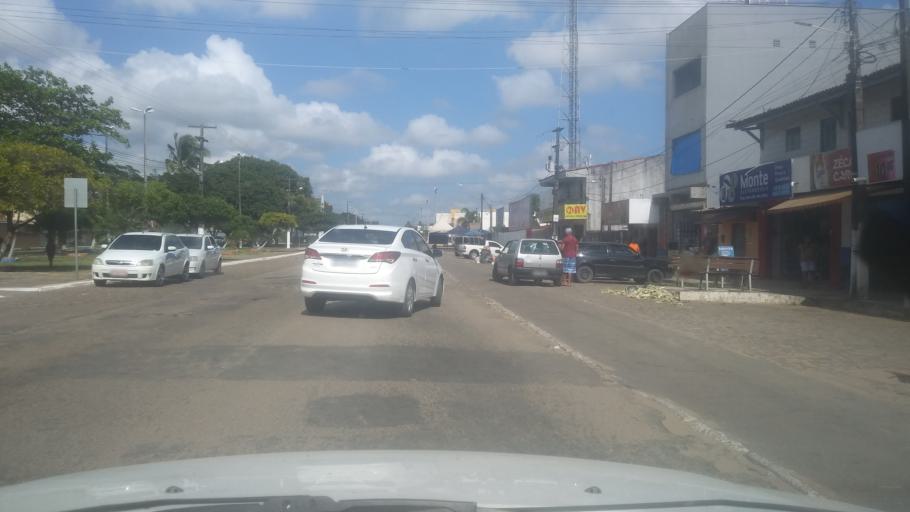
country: BR
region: Rio Grande do Norte
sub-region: Extremoz
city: Extremoz
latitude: -5.7041
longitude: -35.2915
